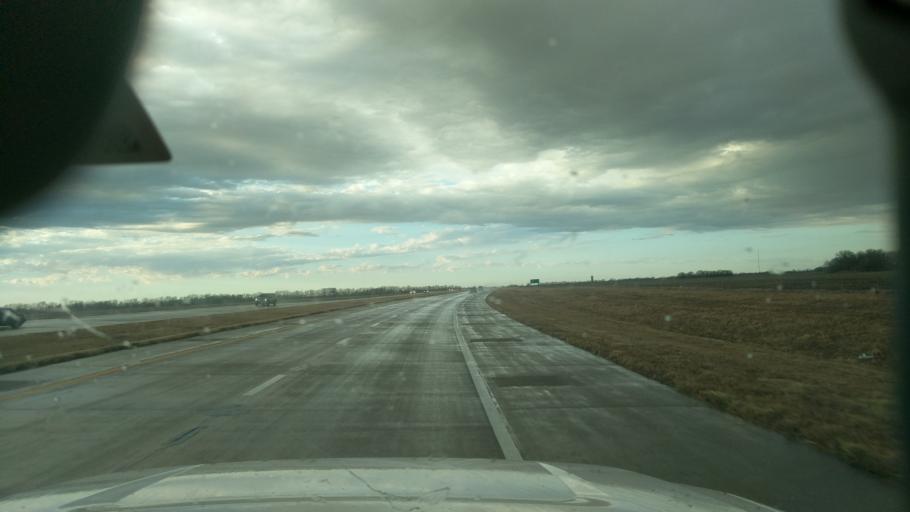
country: US
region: Kansas
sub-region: Harvey County
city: North Newton
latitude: 38.0894
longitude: -97.3569
